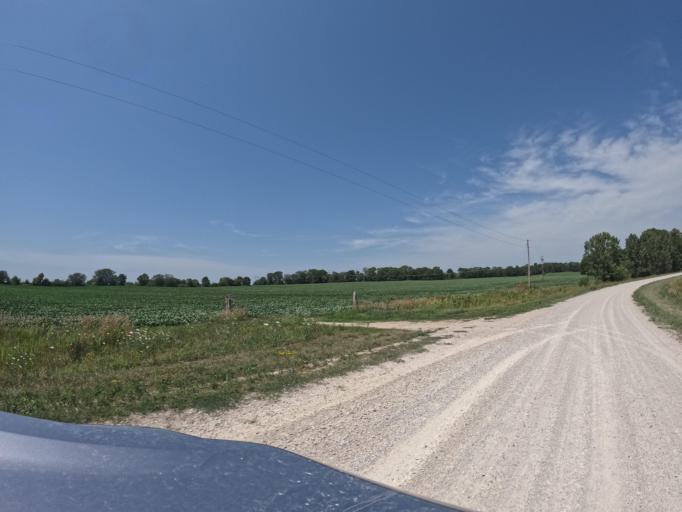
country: US
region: Iowa
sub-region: Henry County
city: Mount Pleasant
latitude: 40.9771
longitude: -91.6595
